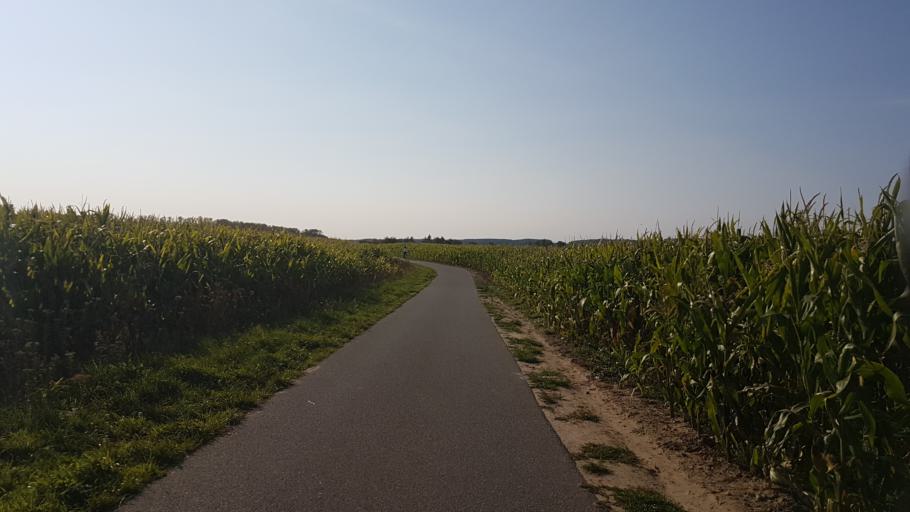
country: DE
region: Mecklenburg-Vorpommern
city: Ostseebad Sellin
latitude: 54.3544
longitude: 13.6621
